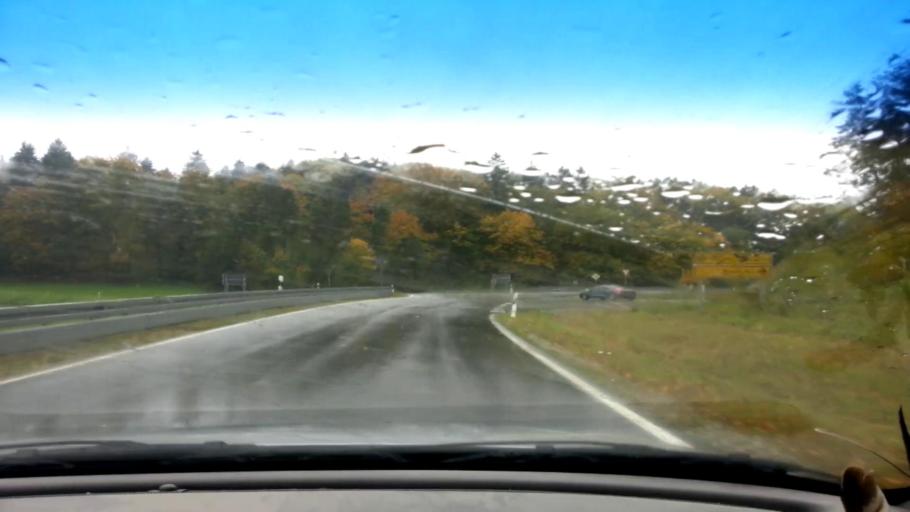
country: DE
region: Bavaria
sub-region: Upper Franconia
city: Heiligenstadt
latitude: 49.8918
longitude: 11.1596
